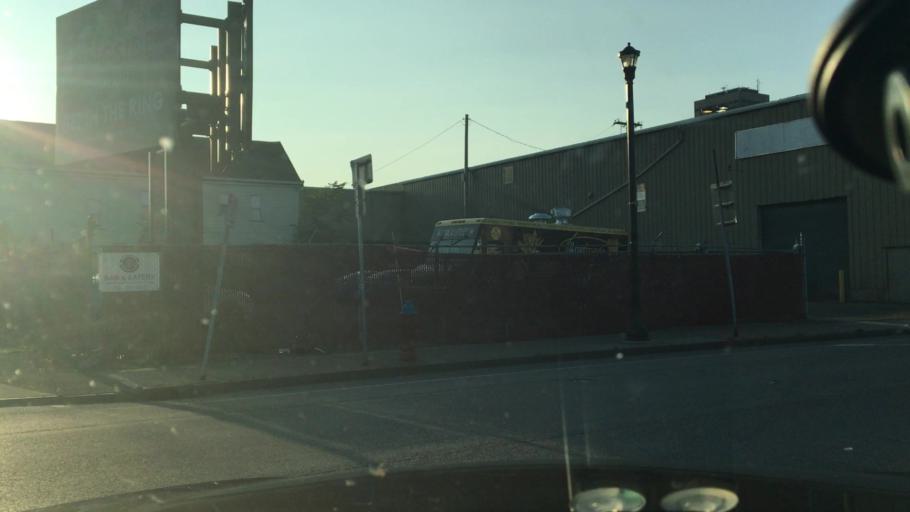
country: US
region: New York
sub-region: Erie County
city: Buffalo
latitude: 42.8731
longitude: -78.8717
